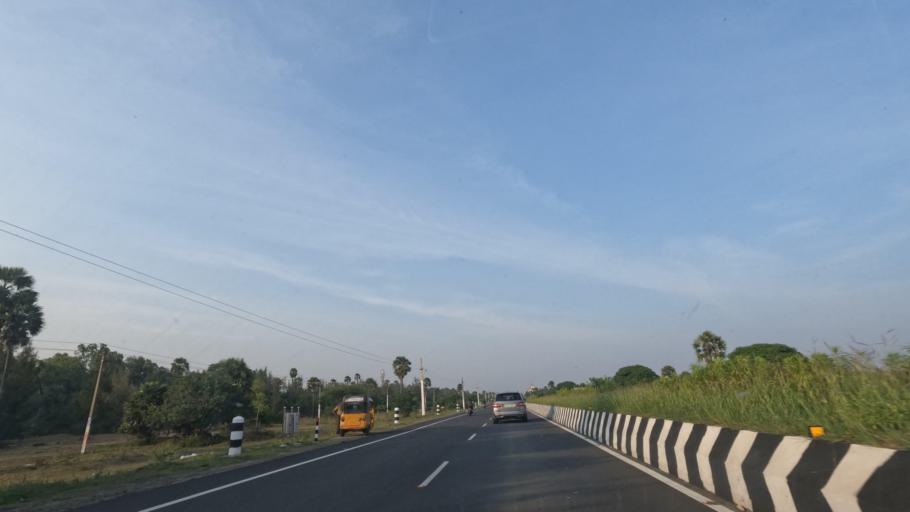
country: IN
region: Tamil Nadu
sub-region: Kancheepuram
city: Mamallapuram
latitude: 12.6773
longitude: 80.2127
